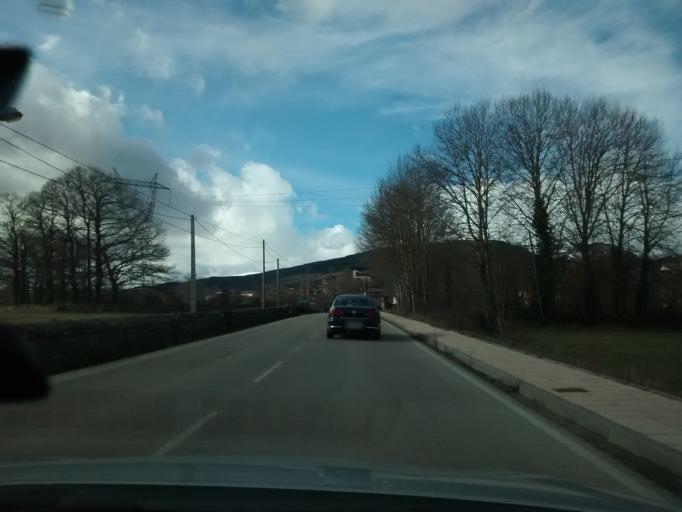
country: ES
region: Castille and Leon
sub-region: Provincia de Burgos
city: Espinosa de los Monteros
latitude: 43.0730
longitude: -3.5350
